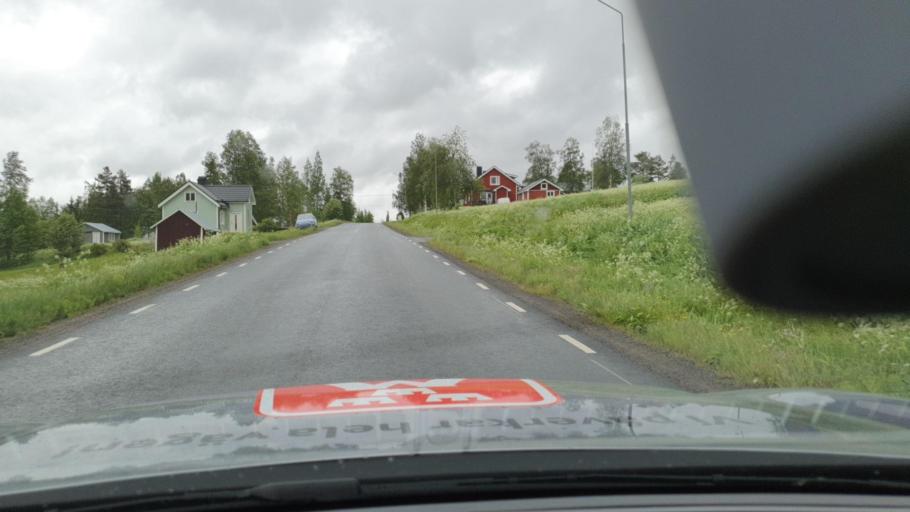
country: FI
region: Lapland
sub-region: Torniolaakso
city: Ylitornio
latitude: 66.1827
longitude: 23.7783
